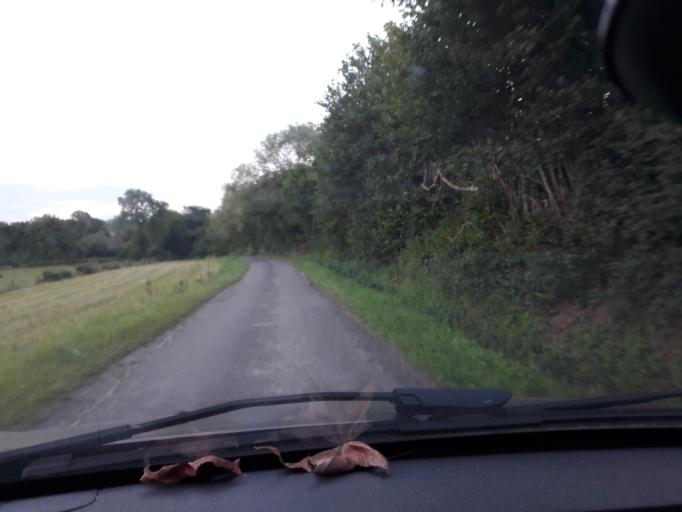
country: BE
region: Wallonia
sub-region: Province du Hainaut
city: Beaumont
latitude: 50.2670
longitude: 4.1898
